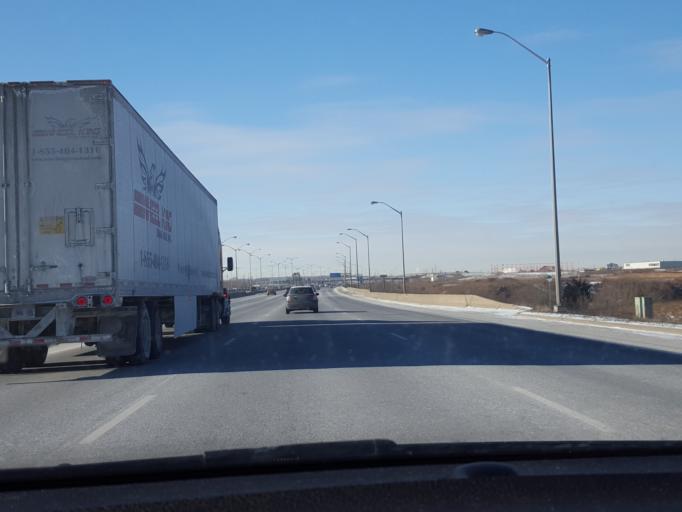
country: CA
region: Ontario
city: Etobicoke
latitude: 43.6555
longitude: -79.6223
